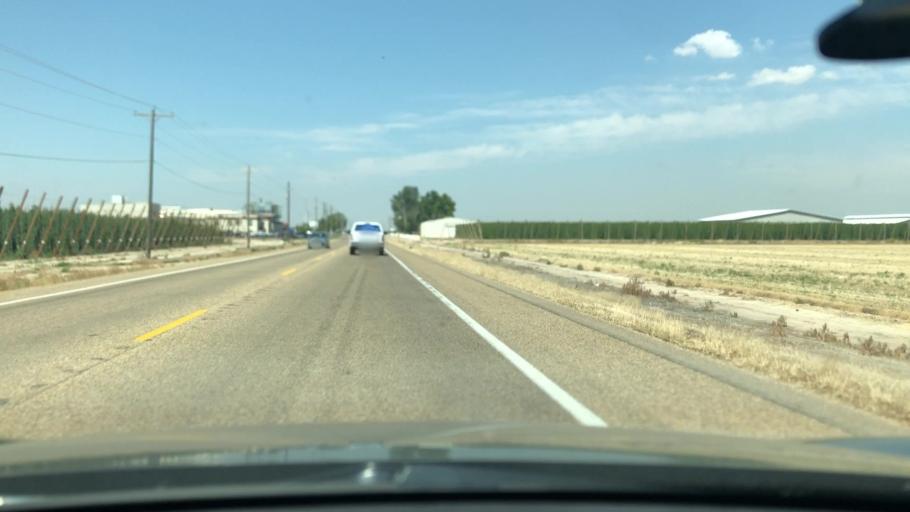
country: US
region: Idaho
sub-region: Canyon County
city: Wilder
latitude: 43.6923
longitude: -116.9120
